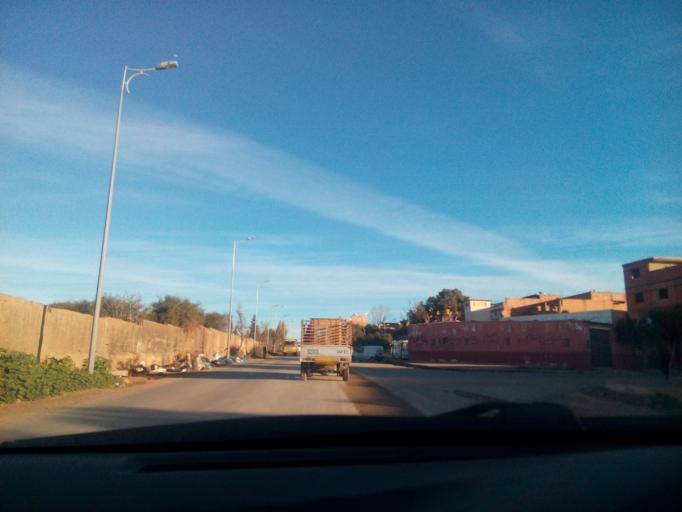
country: DZ
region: Oran
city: Es Senia
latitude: 35.6323
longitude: -0.6741
